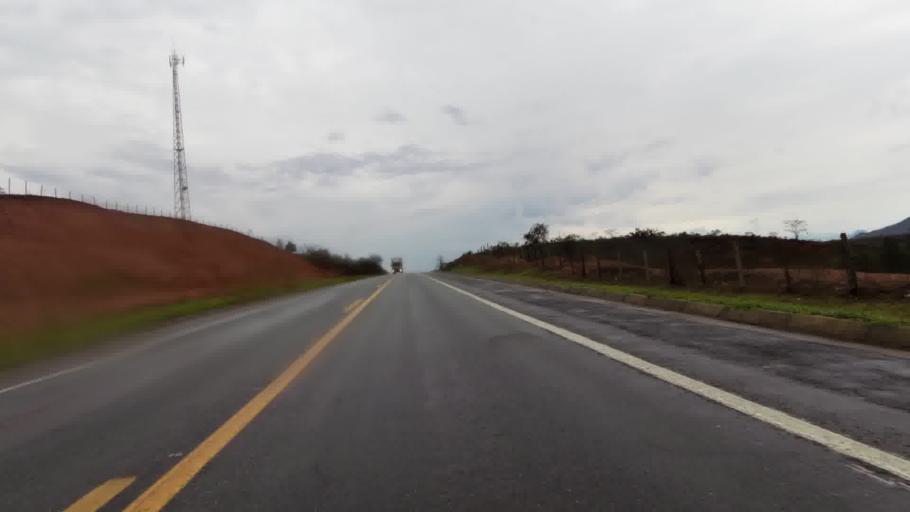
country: BR
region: Rio de Janeiro
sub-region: Campos Dos Goytacazes
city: Campos
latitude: -21.4849
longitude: -41.3401
